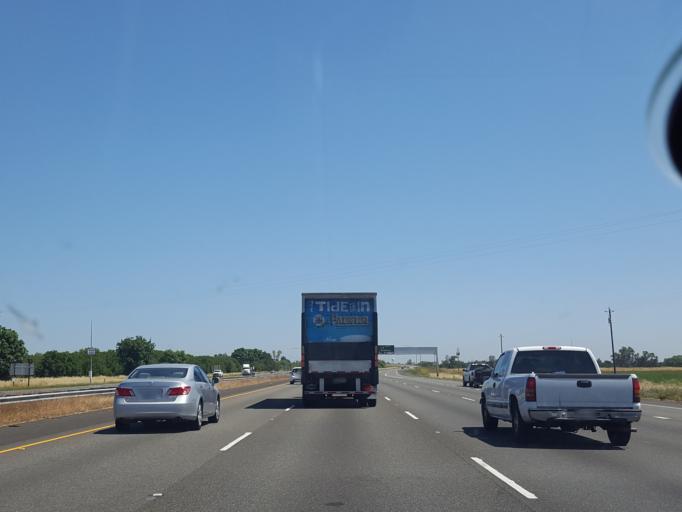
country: US
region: California
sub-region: Yolo County
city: Davis
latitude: 38.5124
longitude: -121.7780
